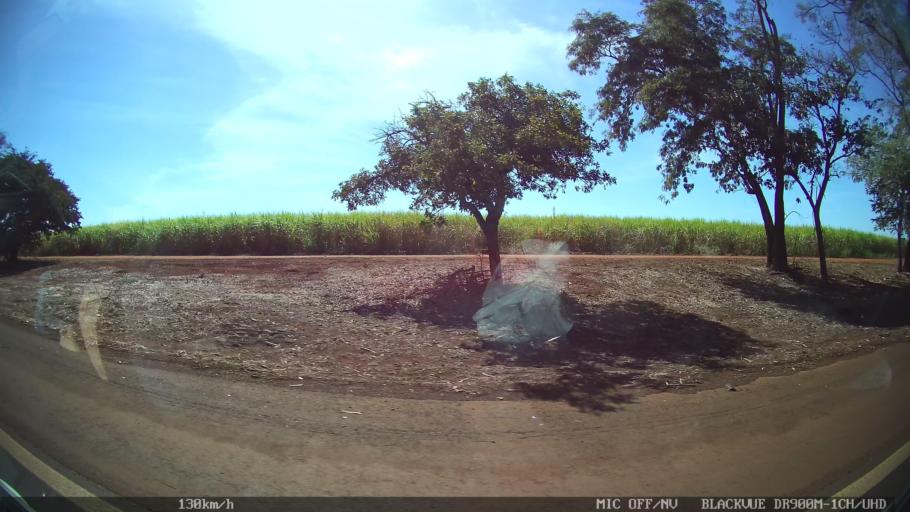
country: BR
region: Sao Paulo
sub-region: Guaira
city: Guaira
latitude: -20.4439
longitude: -48.3021
